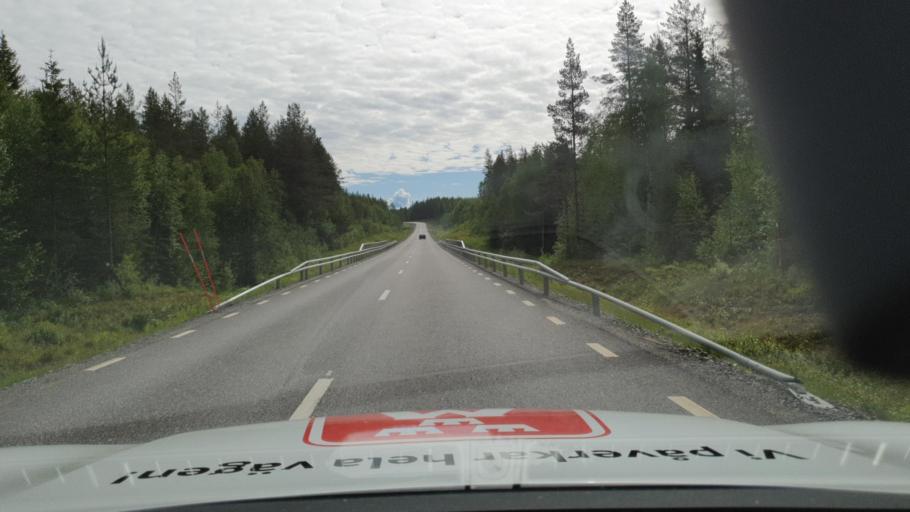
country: SE
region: Vaesterbotten
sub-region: Vindelns Kommun
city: Vindeln
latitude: 64.2498
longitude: 20.0004
